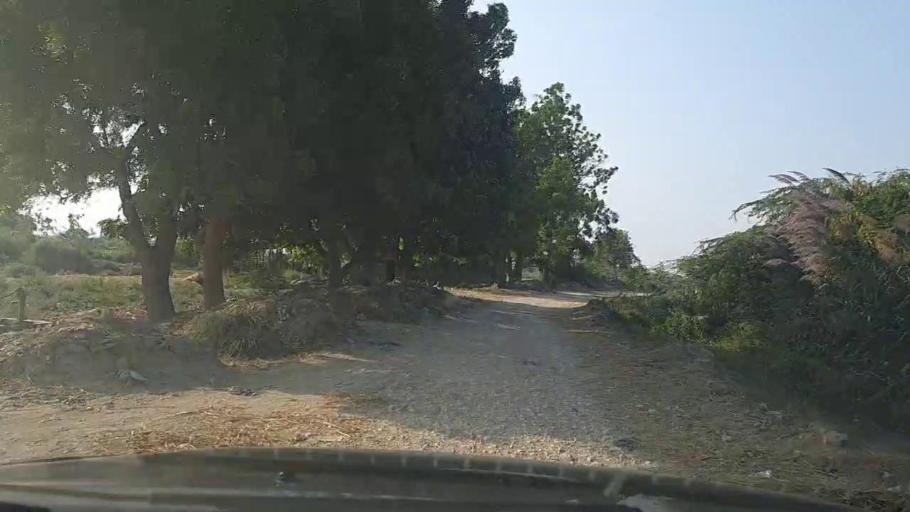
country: PK
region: Sindh
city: Mirpur Sakro
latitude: 24.6357
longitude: 67.7524
